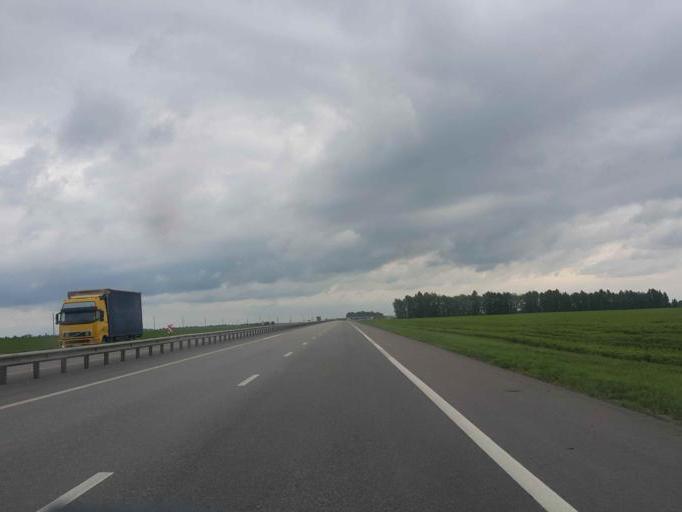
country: RU
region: Tambov
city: Zavoronezhskoye
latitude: 52.8303
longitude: 40.8894
